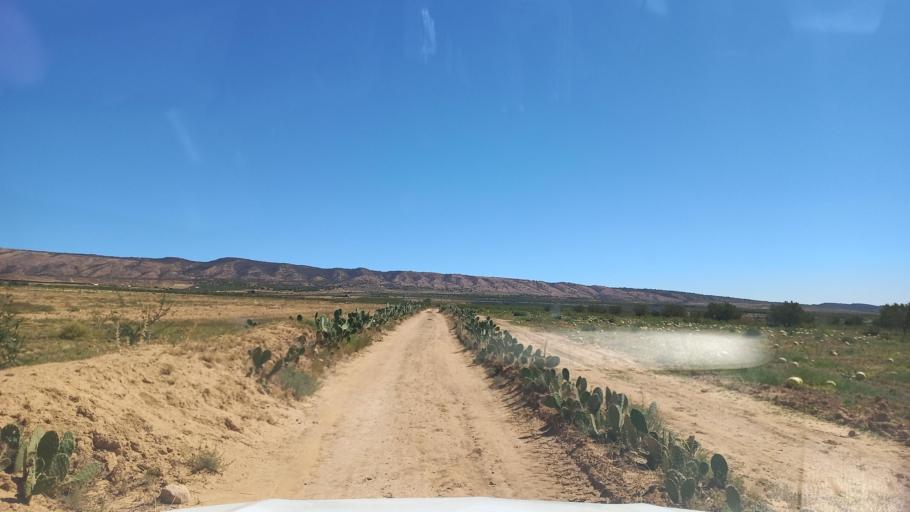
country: TN
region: Al Qasrayn
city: Sbiba
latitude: 35.3493
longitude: 9.1014
